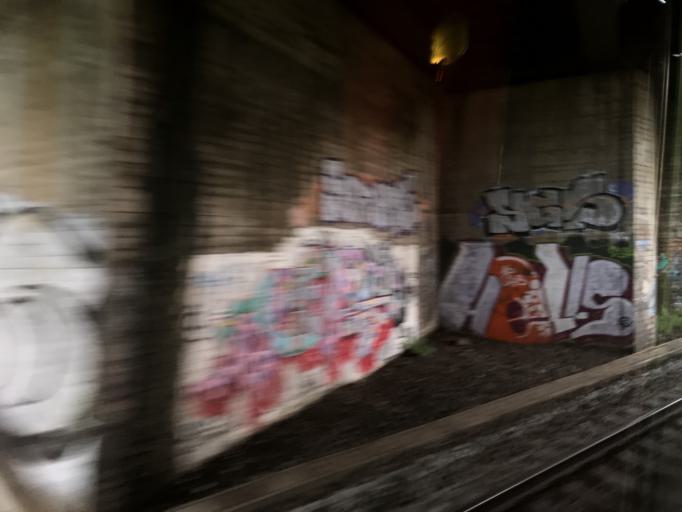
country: DE
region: Bavaria
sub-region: Upper Bavaria
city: Pasing
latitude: 48.1456
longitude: 11.4907
